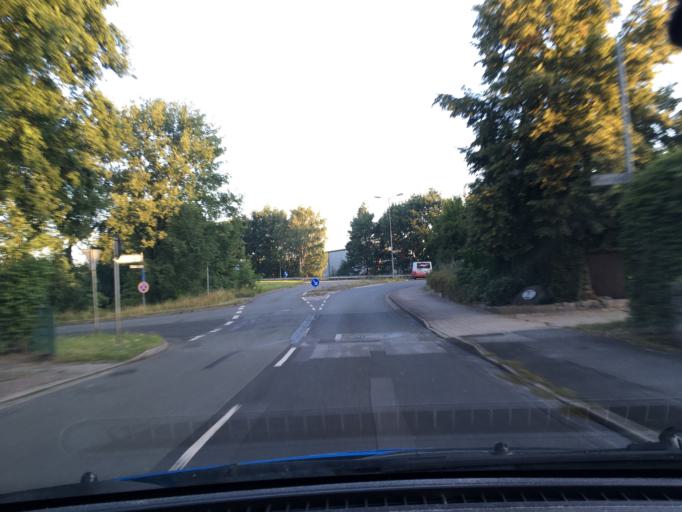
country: DE
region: Lower Saxony
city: Harmstorf
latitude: 53.3855
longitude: 10.0233
